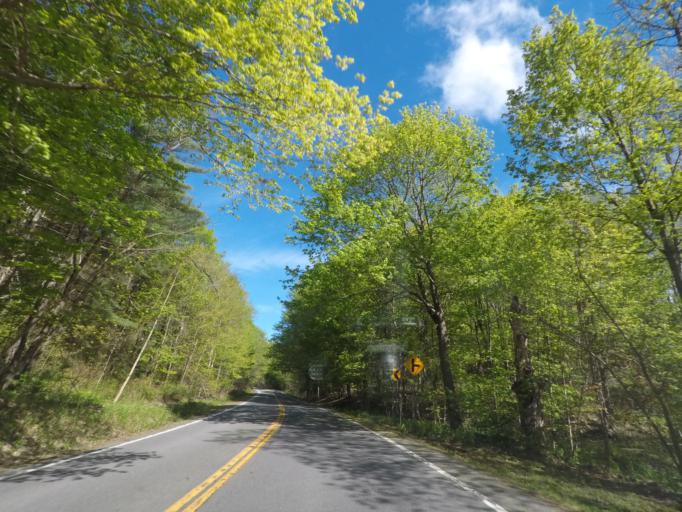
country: US
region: New York
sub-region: Albany County
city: Ravena
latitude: 42.4809
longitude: -73.9254
